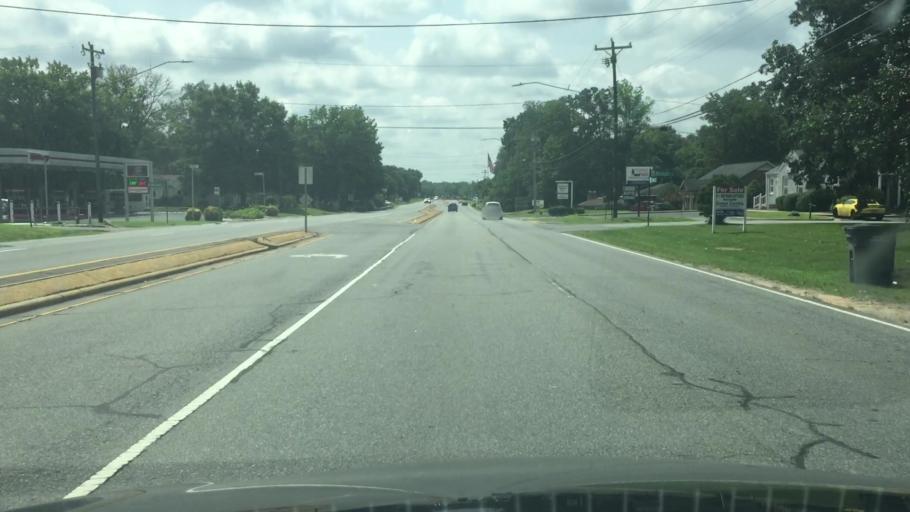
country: US
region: North Carolina
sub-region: Cabarrus County
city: Kannapolis
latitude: 35.4625
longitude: -80.6092
